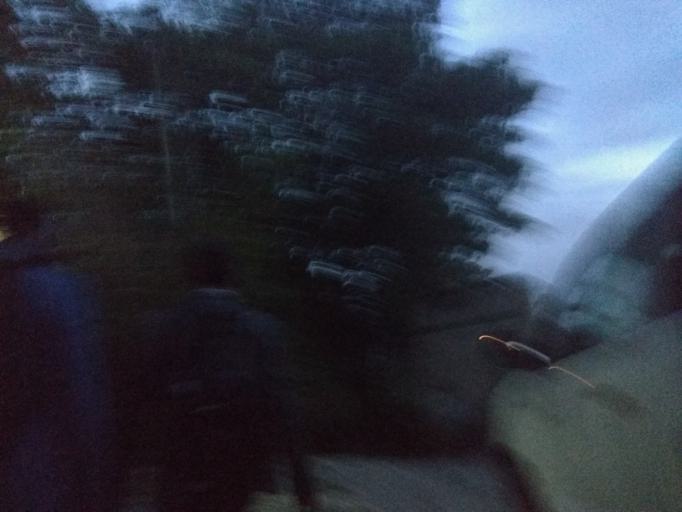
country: ET
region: Oromiya
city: Hagere Hiywet
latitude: 8.9808
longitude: 37.8529
